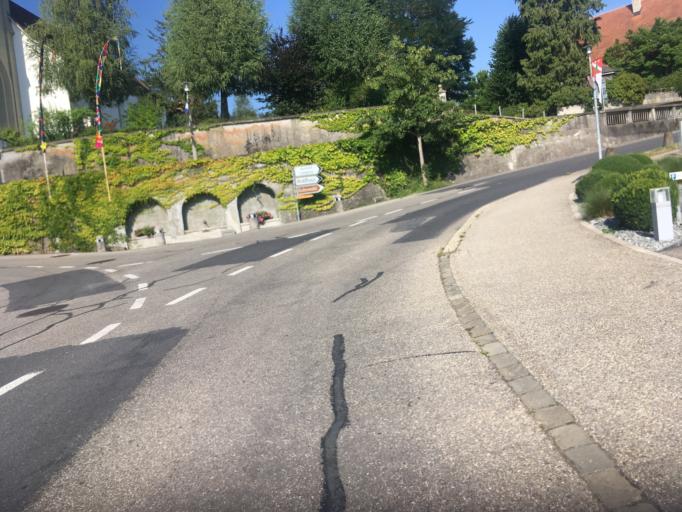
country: CH
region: Bern
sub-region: Emmental District
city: Lutzelfluh
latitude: 47.0078
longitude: 7.6865
